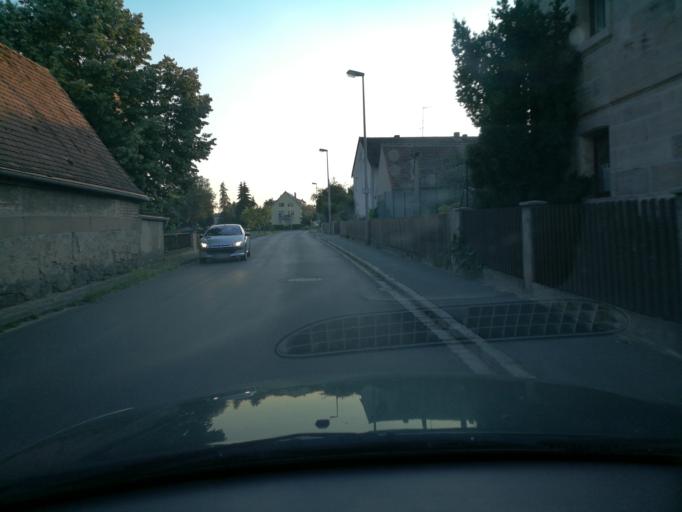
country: DE
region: Bavaria
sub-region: Regierungsbezirk Mittelfranken
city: Hessdorf
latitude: 49.6152
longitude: 10.9069
